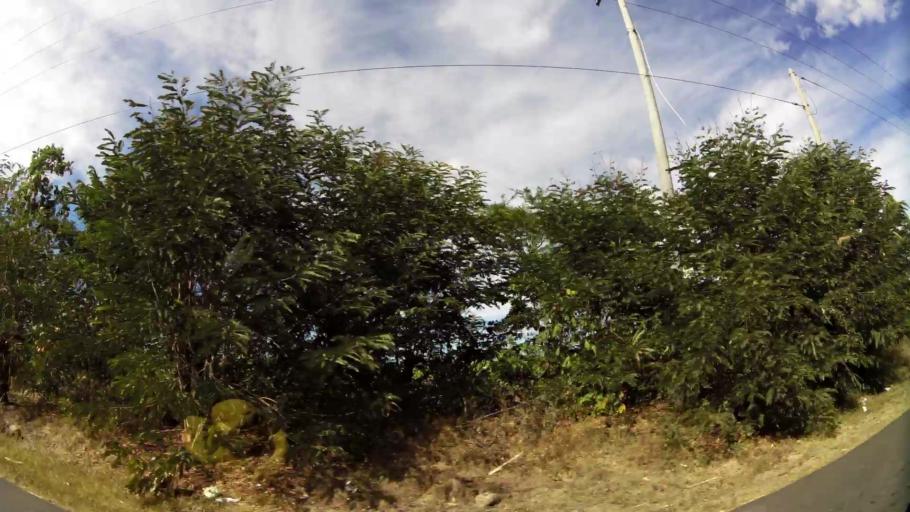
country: SV
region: San Salvador
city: Aguilares
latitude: 13.9618
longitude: -89.1282
